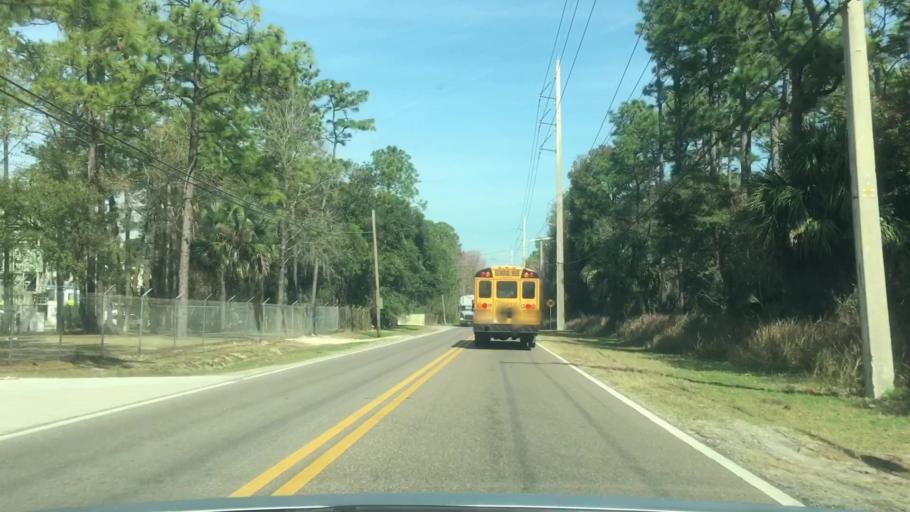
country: US
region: Florida
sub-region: Duval County
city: Jacksonville
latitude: 30.4301
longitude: -81.5607
